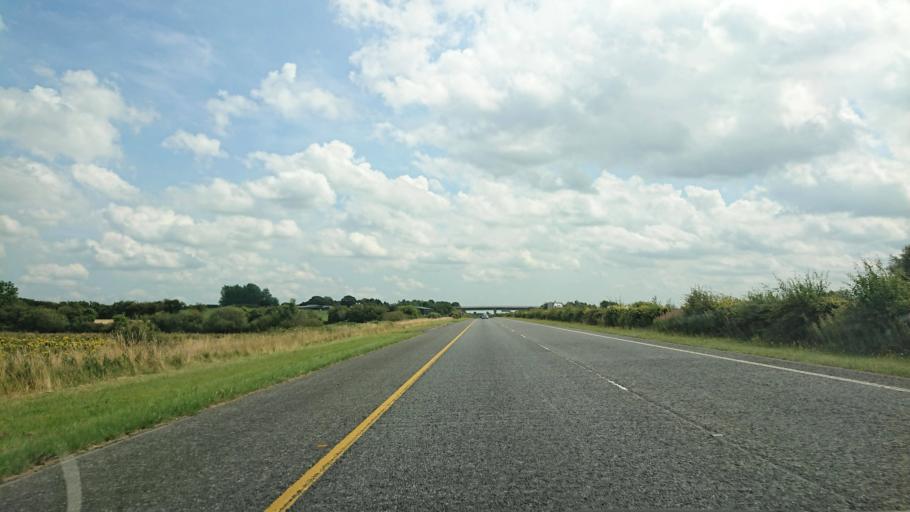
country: IE
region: Leinster
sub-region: An Iarmhi
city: Kinnegad
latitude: 53.4439
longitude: -7.0442
